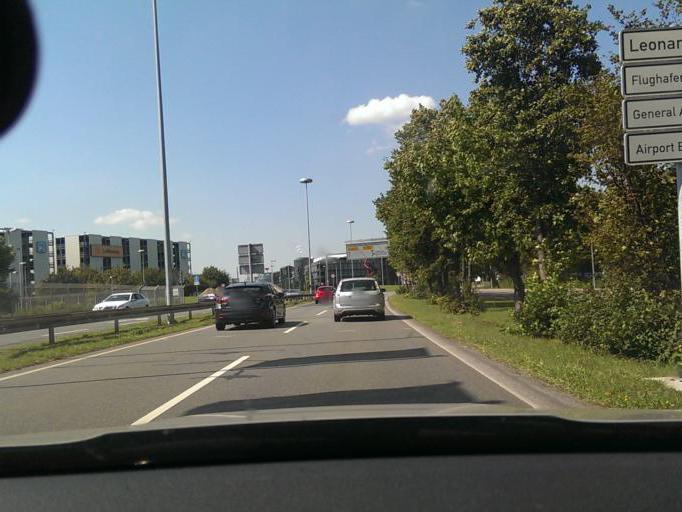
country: DE
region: Lower Saxony
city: Langenhagen
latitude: 52.4587
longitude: 9.7075
